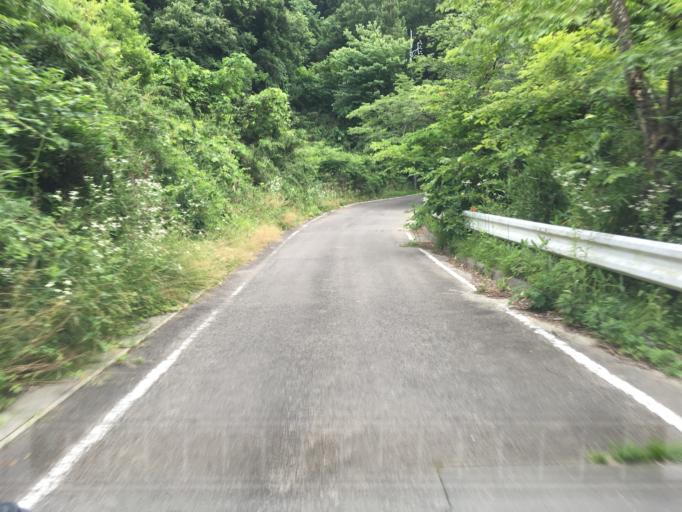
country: JP
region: Fukushima
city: Nihommatsu
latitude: 37.6399
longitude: 140.5279
